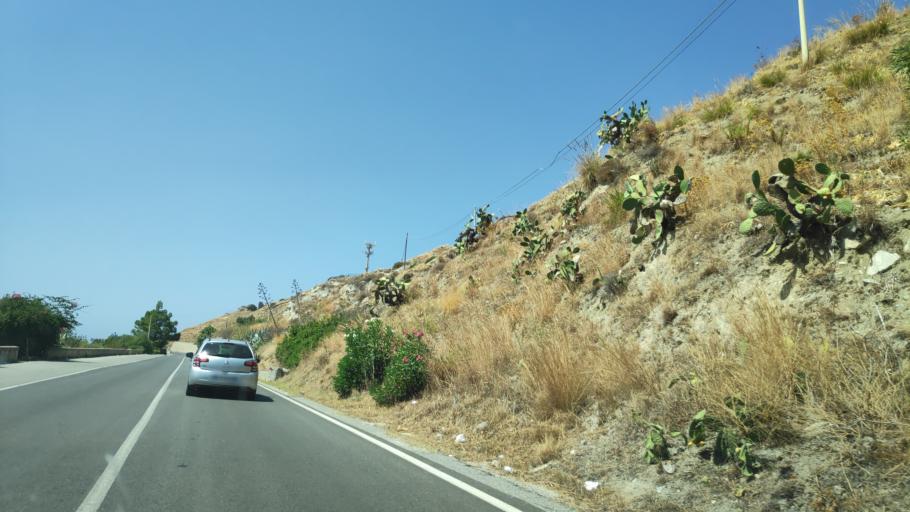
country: IT
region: Calabria
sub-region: Provincia di Reggio Calabria
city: Palizzi Marina
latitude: 37.9189
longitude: 16.0028
